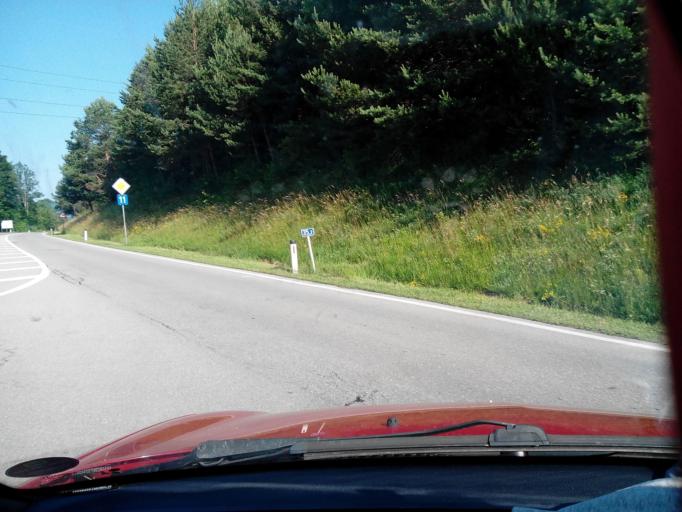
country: AT
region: Lower Austria
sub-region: Politischer Bezirk Baden
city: Heiligenkreuz
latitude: 48.0541
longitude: 16.1089
